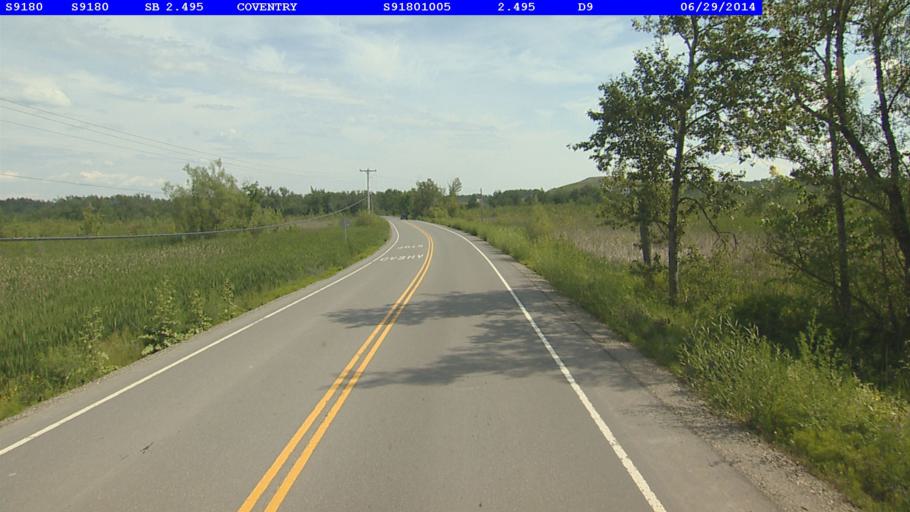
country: US
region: Vermont
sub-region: Orleans County
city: Newport
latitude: 44.9219
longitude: -72.2279
